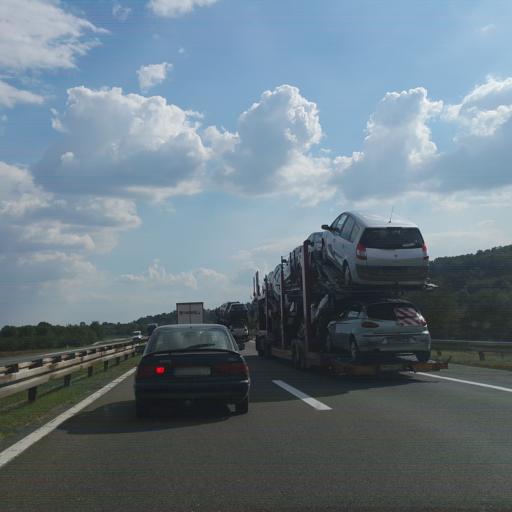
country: RS
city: Lugavcina
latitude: 44.4393
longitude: 21.0499
